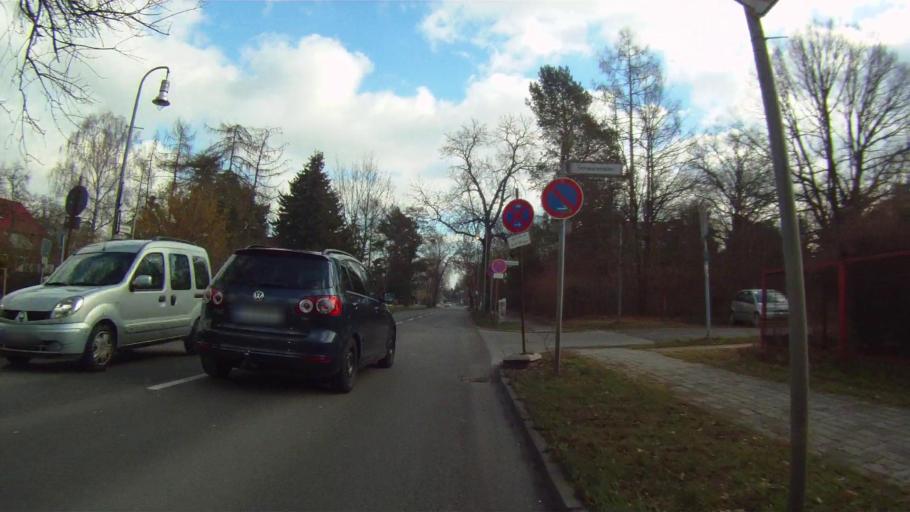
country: DE
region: Berlin
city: Biesdorf
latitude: 52.4933
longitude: 13.5646
